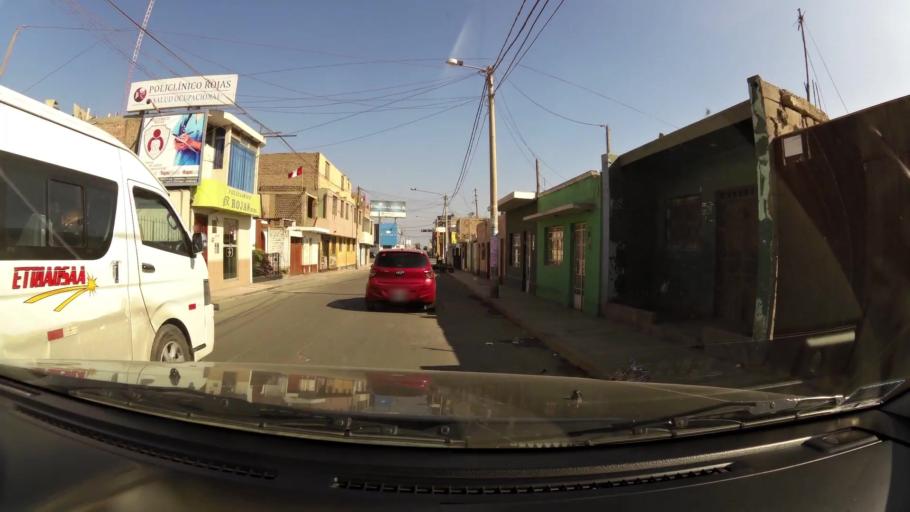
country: PE
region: Ica
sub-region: Provincia de Chincha
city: Chincha Alta
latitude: -13.4233
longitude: -76.1348
